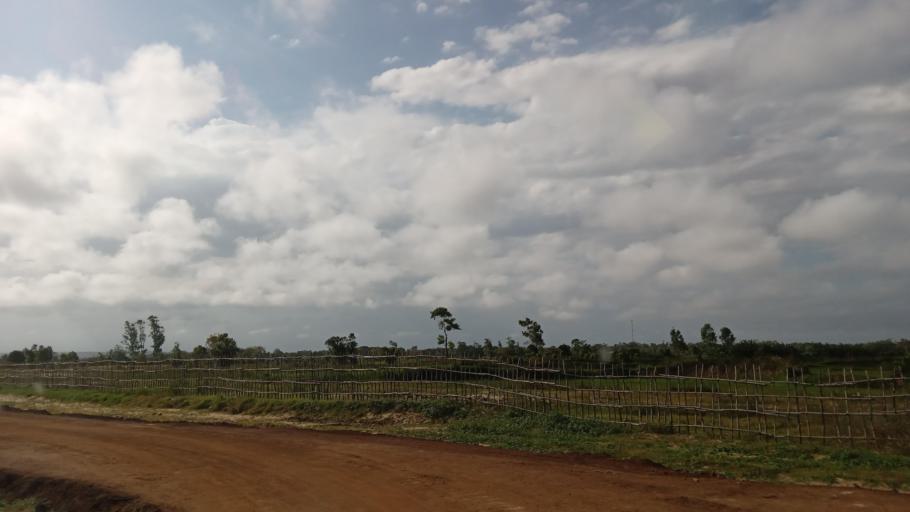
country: MG
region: Atsimo-Atsinanana
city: Vohipaho
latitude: -23.8117
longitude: 47.5498
